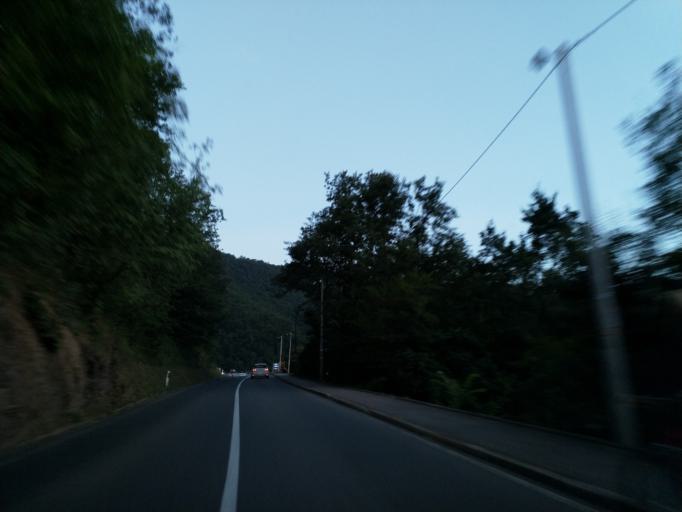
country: RS
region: Central Serbia
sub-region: Rasinski Okrug
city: Aleksandrovac
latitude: 43.3755
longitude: 21.0414
